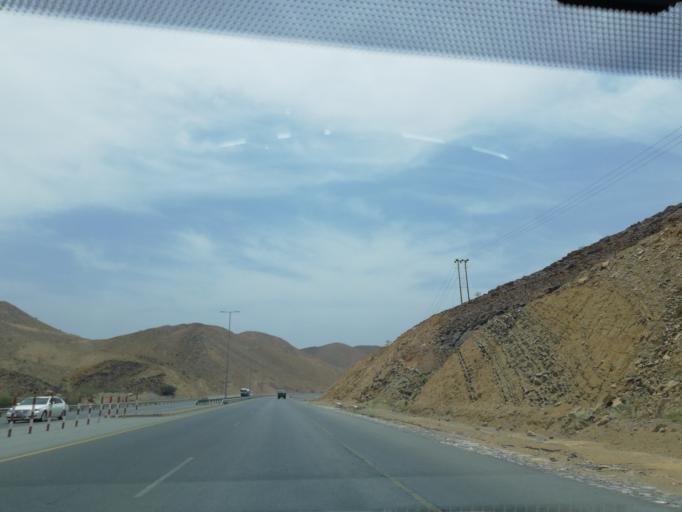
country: OM
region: Muhafazat ad Dakhiliyah
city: Izki
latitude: 22.8917
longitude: 57.7169
